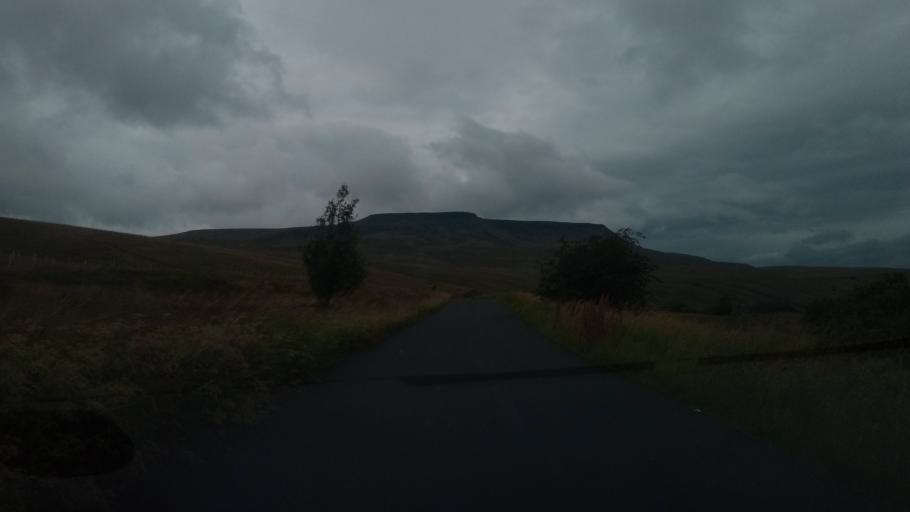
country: GB
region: England
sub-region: Cumbria
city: Kirkby Stephen
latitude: 54.3624
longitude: -2.3446
